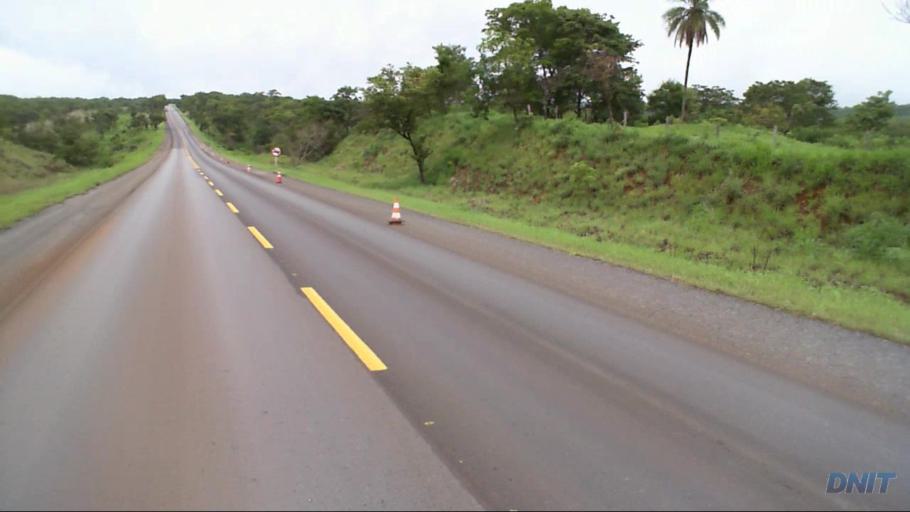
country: BR
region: Goias
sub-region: Padre Bernardo
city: Padre Bernardo
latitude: -15.1857
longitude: -48.4320
